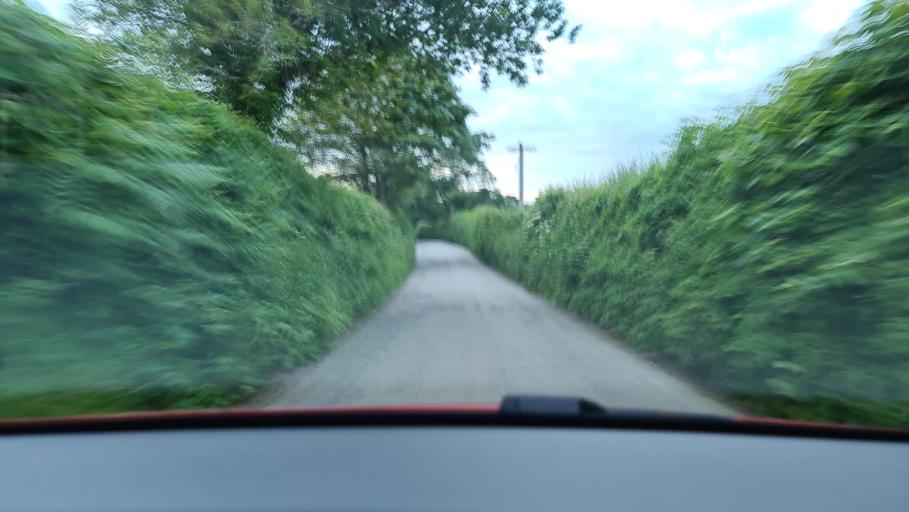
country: GB
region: England
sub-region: Cornwall
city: Looe
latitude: 50.4034
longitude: -4.4226
